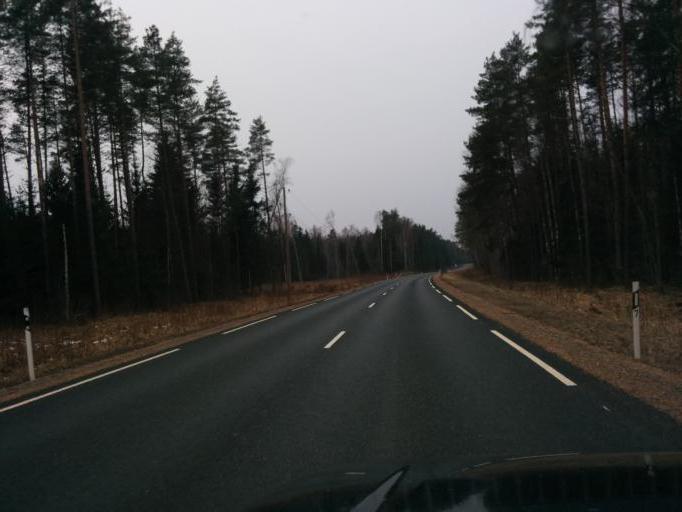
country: LV
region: Ikskile
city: Ikskile
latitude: 56.8001
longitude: 24.5302
